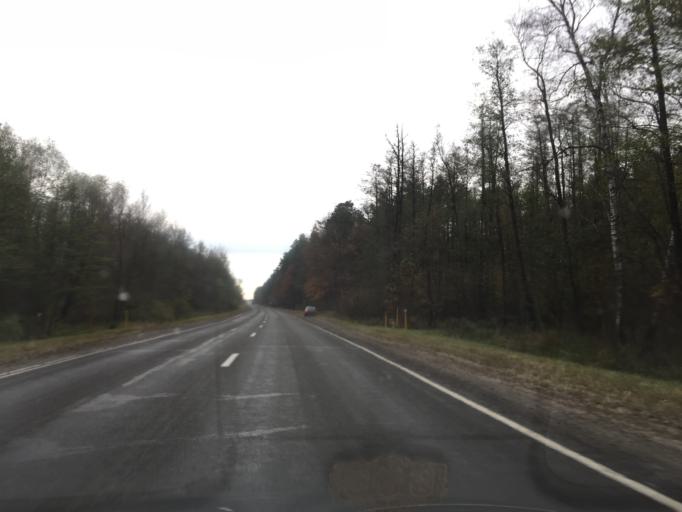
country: BY
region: Gomel
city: Gomel
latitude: 52.4003
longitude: 30.8291
